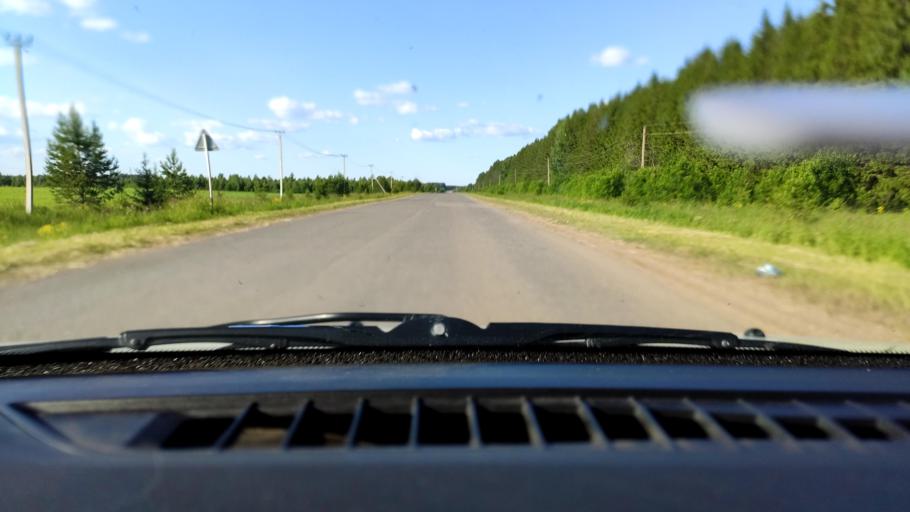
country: RU
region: Perm
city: Uinskoye
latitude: 57.1032
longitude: 56.6566
